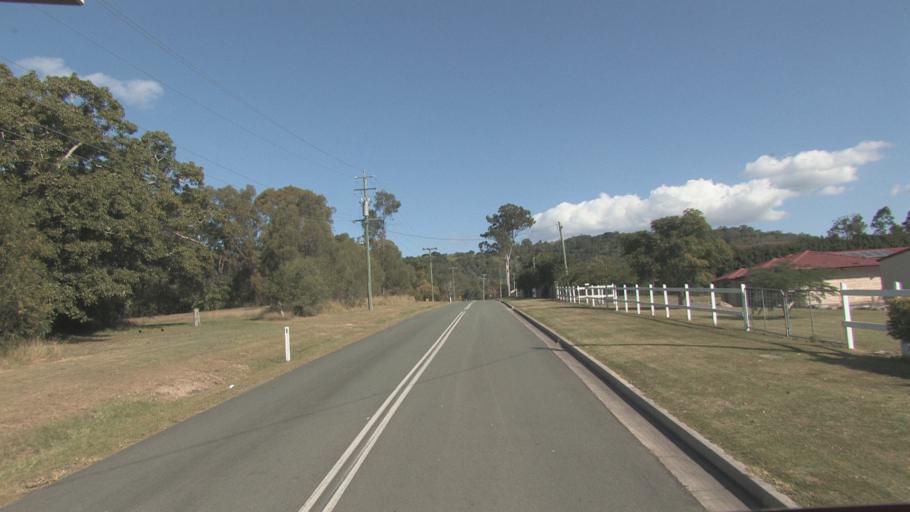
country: AU
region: Queensland
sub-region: Logan
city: Windaroo
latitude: -27.7379
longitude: 153.1739
